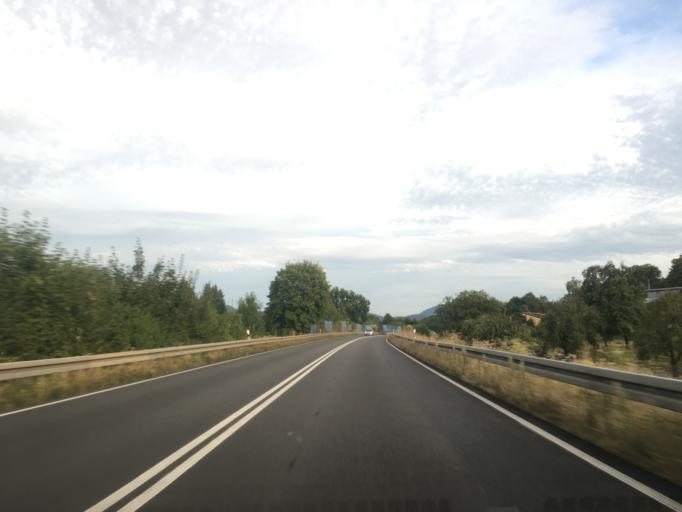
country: DE
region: Baden-Wuerttemberg
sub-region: Regierungsbezirk Stuttgart
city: Bempflingen
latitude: 48.5740
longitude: 9.2581
